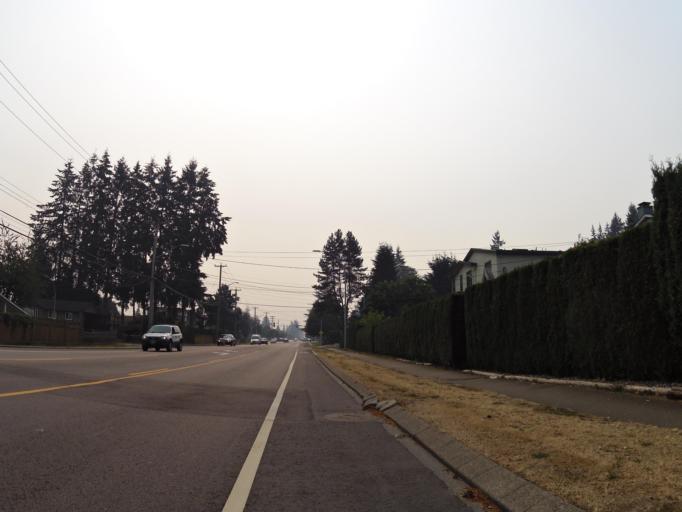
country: CA
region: British Columbia
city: Surrey
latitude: 49.1207
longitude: -122.8565
